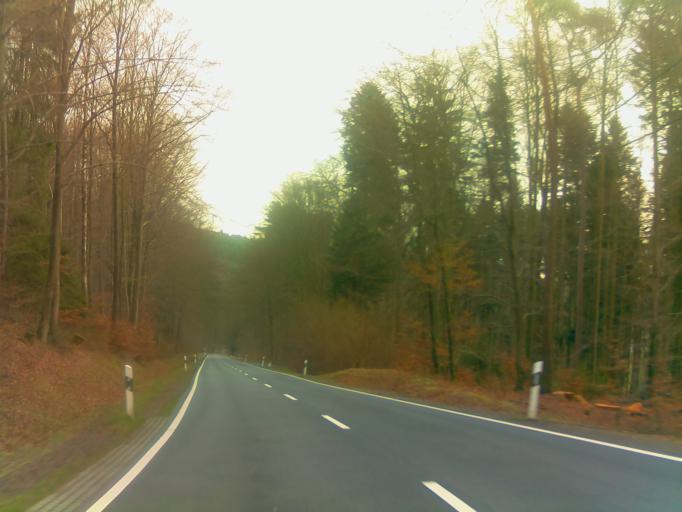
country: DE
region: Hesse
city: Reichelsheim
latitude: 49.6532
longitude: 8.8751
